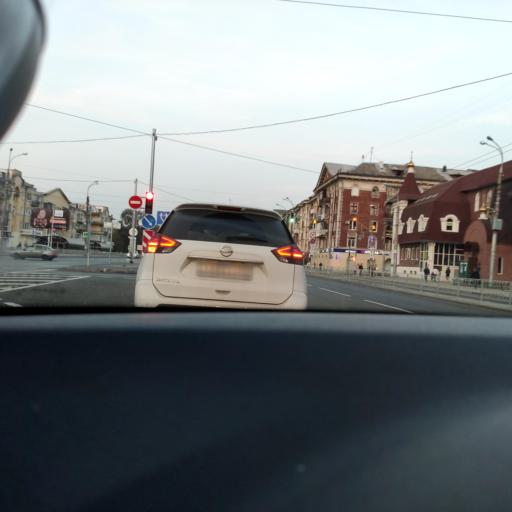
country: RU
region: Samara
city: Samara
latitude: 53.2126
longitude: 50.2481
